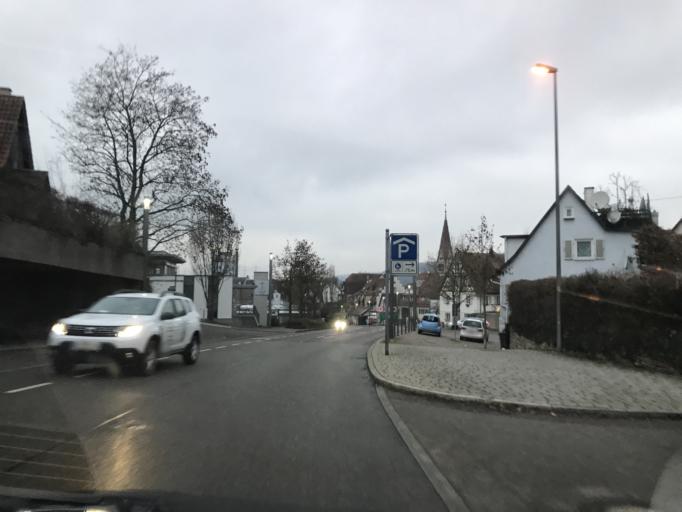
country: DE
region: Baden-Wuerttemberg
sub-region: Regierungsbezirk Stuttgart
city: Plochingen
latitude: 48.7091
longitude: 9.4192
